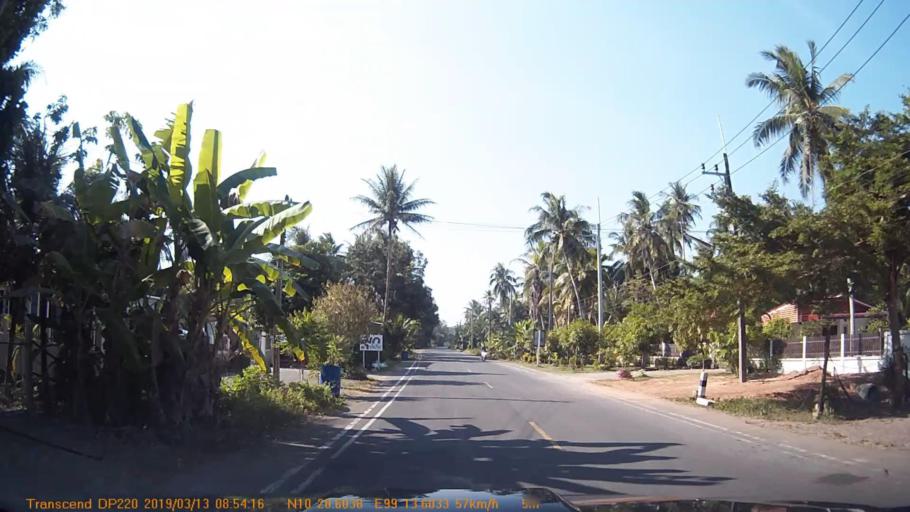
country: TH
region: Chumphon
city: Chumphon
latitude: 10.4765
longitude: 99.2267
